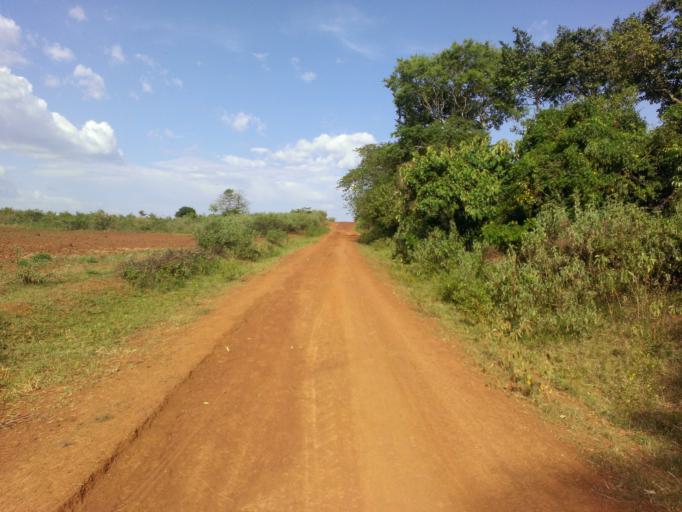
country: UG
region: Eastern Region
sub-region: Busia District
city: Busia
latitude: 0.5489
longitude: 34.0161
